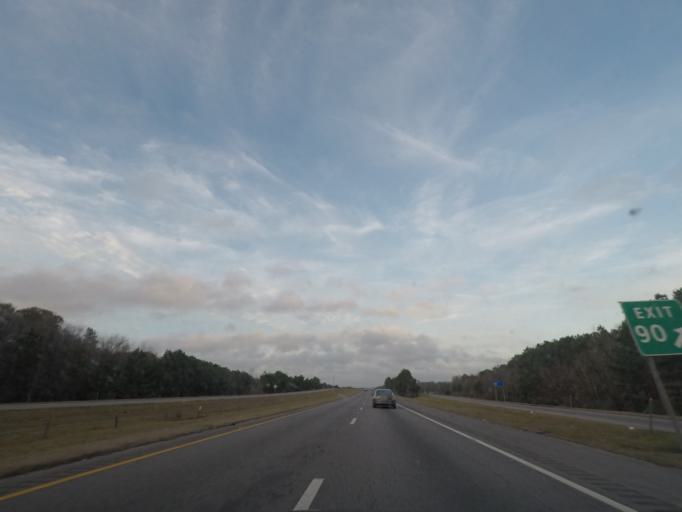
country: US
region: South Carolina
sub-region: Orangeburg County
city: Holly Hill
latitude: 33.3787
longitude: -80.5203
